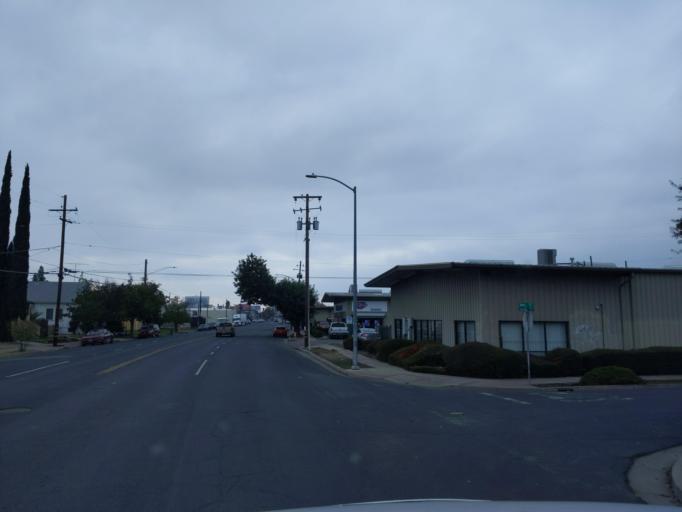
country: US
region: California
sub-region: San Joaquin County
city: August
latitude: 37.9594
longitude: -121.2692
